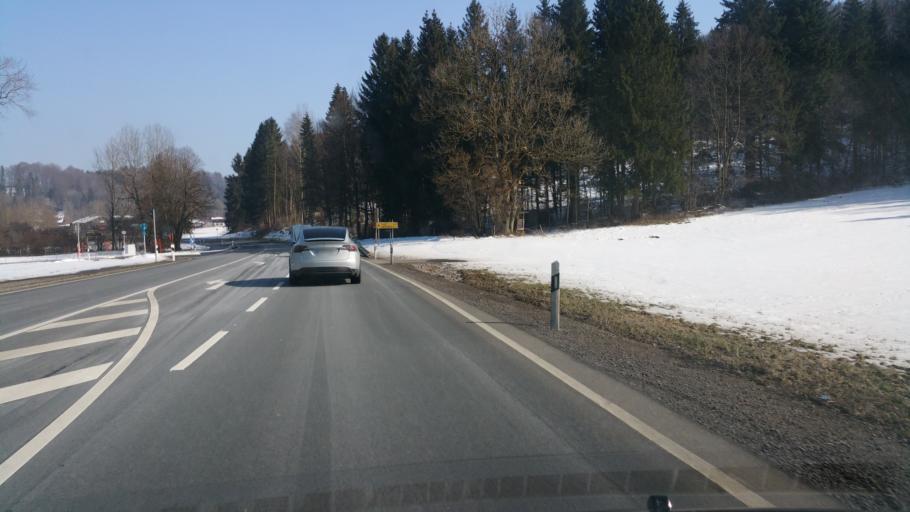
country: DE
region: Bavaria
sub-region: Upper Bavaria
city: Miesbach
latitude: 47.8062
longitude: 11.8726
